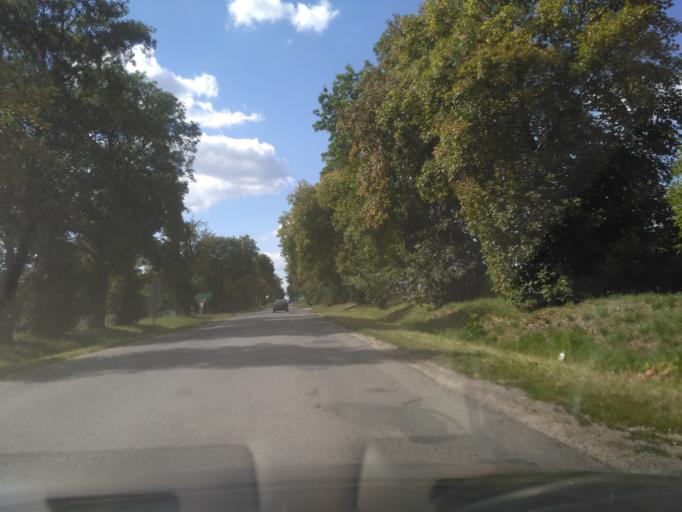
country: PL
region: Lublin Voivodeship
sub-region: Powiat swidnicki
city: Swidnik
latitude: 51.2137
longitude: 22.6401
